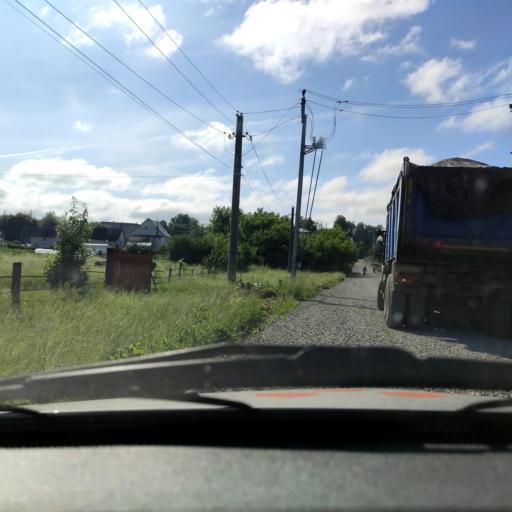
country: RU
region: Bashkortostan
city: Iglino
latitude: 54.7986
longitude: 56.3031
